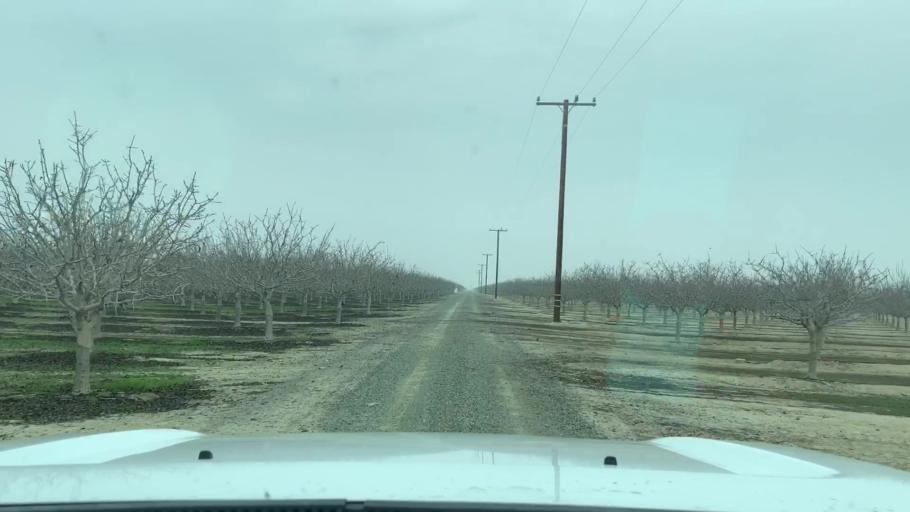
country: US
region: California
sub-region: Tulare County
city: Earlimart
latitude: 35.8202
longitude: -119.3396
